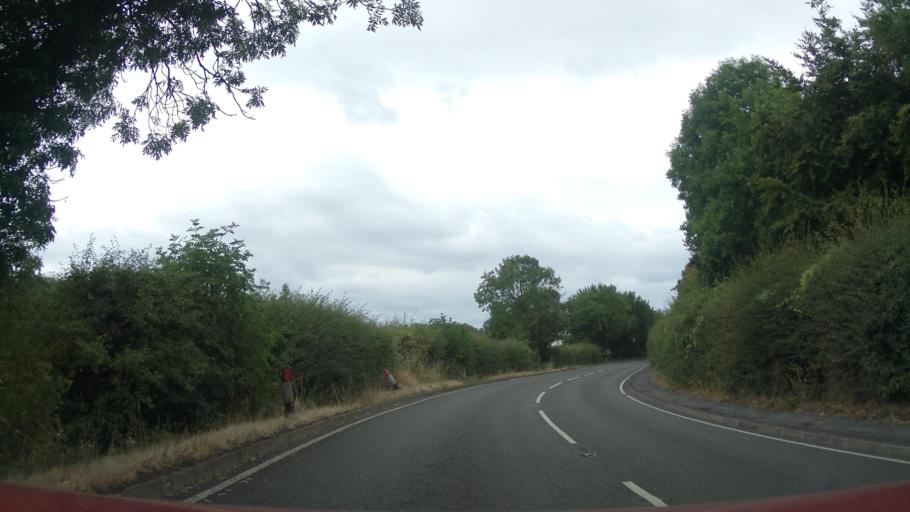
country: GB
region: England
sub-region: Derbyshire
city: Borrowash
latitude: 52.9076
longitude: -1.3567
